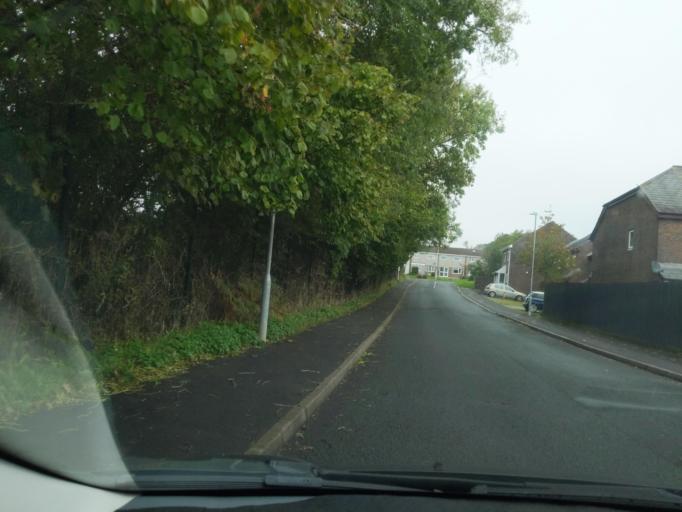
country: GB
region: England
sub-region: Devon
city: Plympton
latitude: 50.4114
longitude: -4.0957
